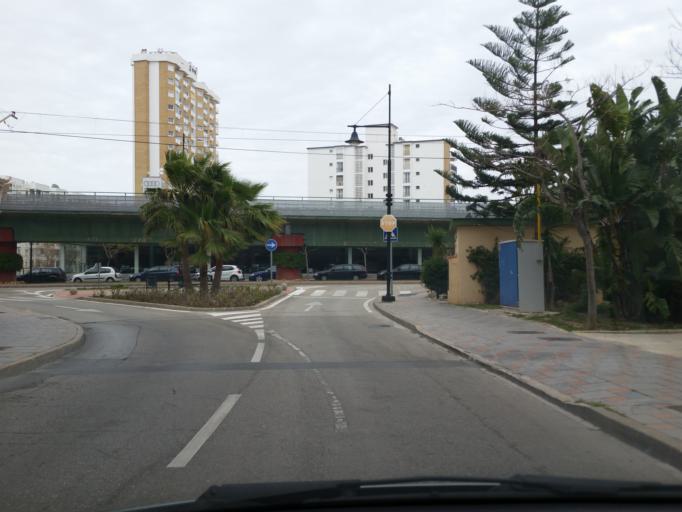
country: ES
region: Andalusia
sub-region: Provincia de Malaga
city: Fuengirola
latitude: 36.5573
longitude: -4.6134
